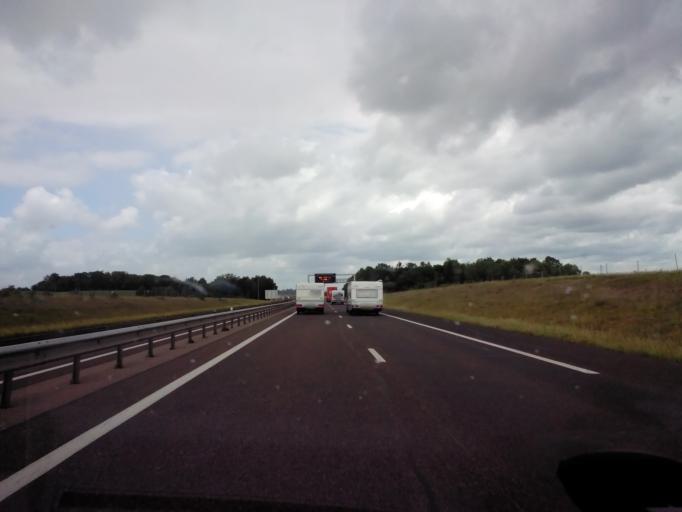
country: FR
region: Lorraine
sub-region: Departement de Meurthe-et-Moselle
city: Blenod-les-Toul
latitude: 48.6099
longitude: 5.8862
